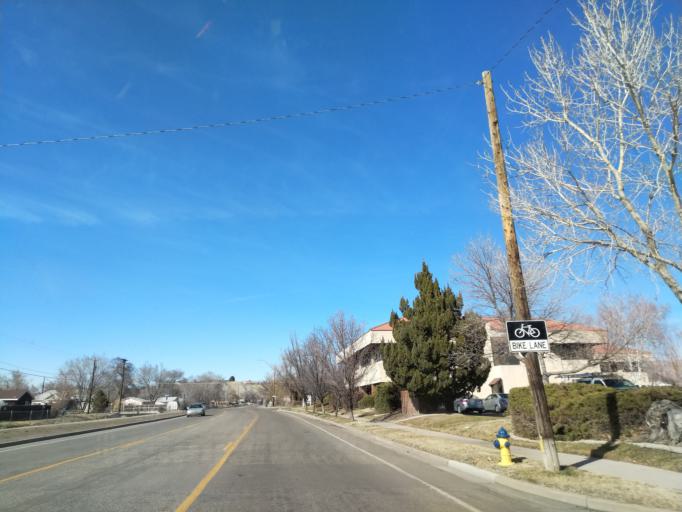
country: US
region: Colorado
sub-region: Mesa County
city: Grand Junction
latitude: 39.0799
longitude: -108.5336
